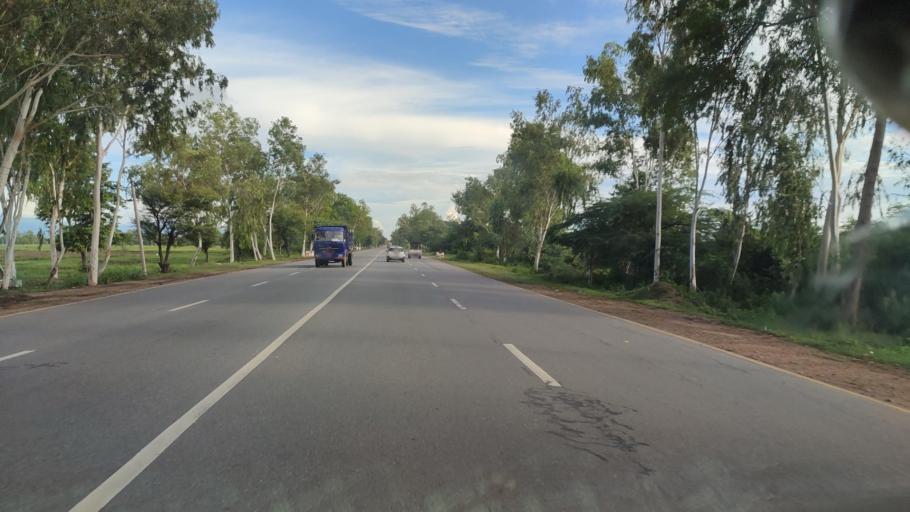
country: MM
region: Mandalay
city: Yamethin
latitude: 20.1694
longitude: 96.1890
